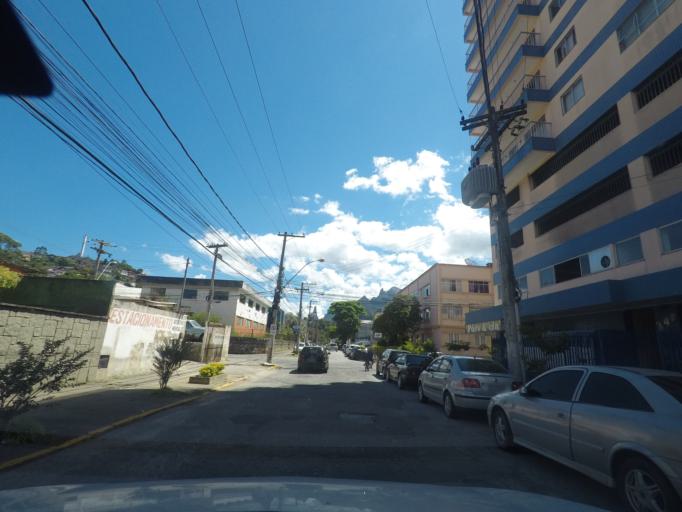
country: BR
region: Rio de Janeiro
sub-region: Teresopolis
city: Teresopolis
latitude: -22.4183
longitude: -42.9722
